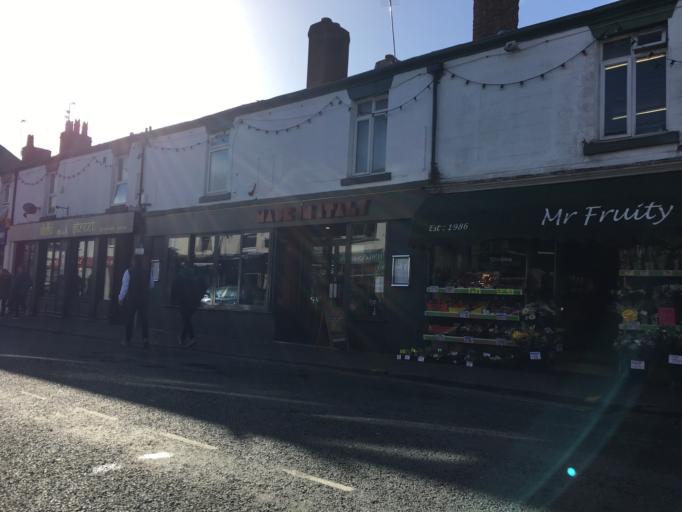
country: GB
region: England
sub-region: Cheshire West and Chester
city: Hoole
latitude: 53.1995
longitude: -2.8764
